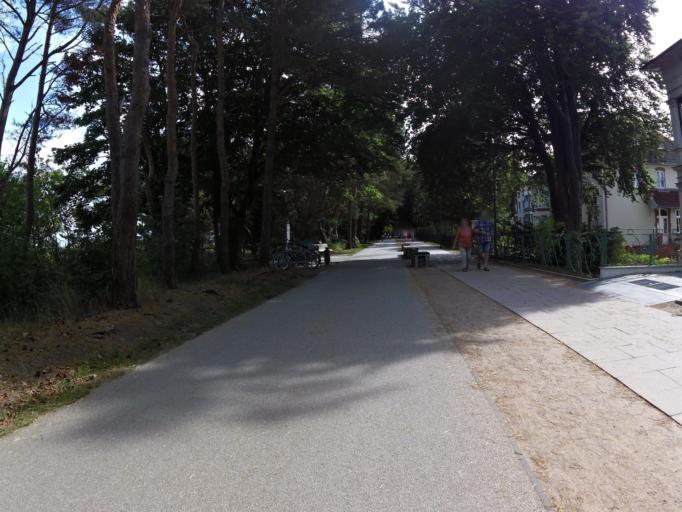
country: DE
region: Mecklenburg-Vorpommern
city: Seebad Bansin
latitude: 53.9651
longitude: 14.1556
